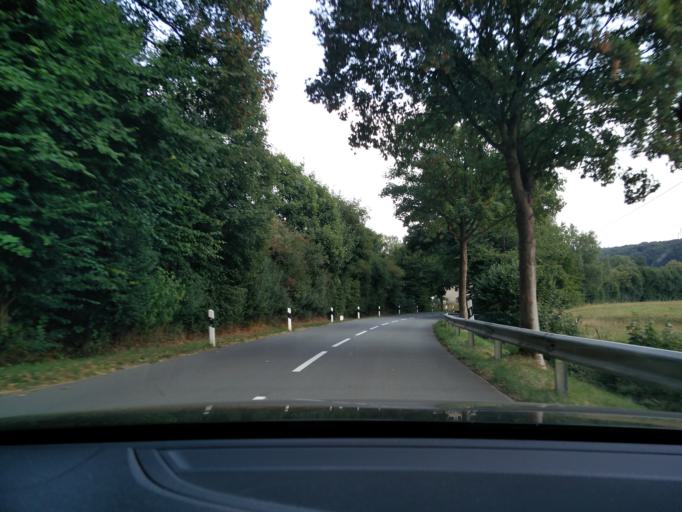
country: DE
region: North Rhine-Westphalia
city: Lichtenau
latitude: 51.6762
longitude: 8.9153
